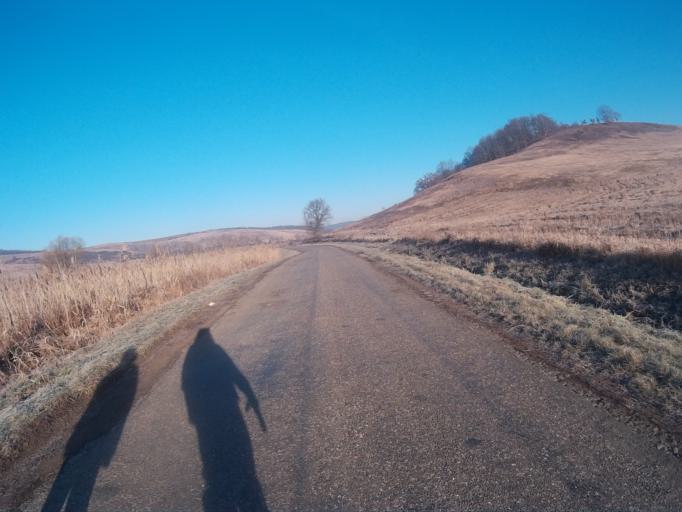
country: HU
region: Borsod-Abauj-Zemplen
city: Putnok
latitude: 48.3608
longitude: 20.4291
